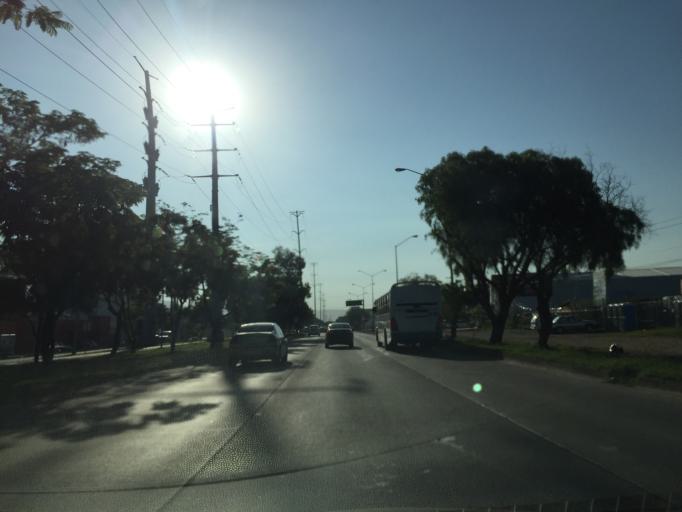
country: MX
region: Guanajuato
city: Leon
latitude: 21.1480
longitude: -101.6583
